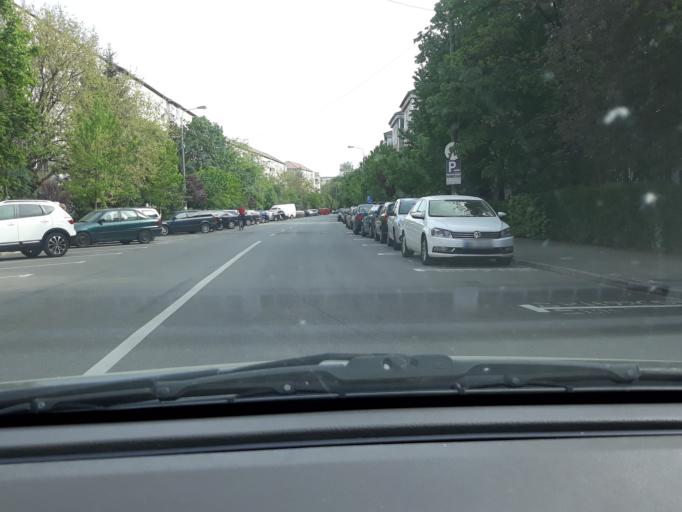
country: RO
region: Bihor
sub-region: Comuna Sanmartin
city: Sanmartin
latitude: 47.0326
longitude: 21.9582
